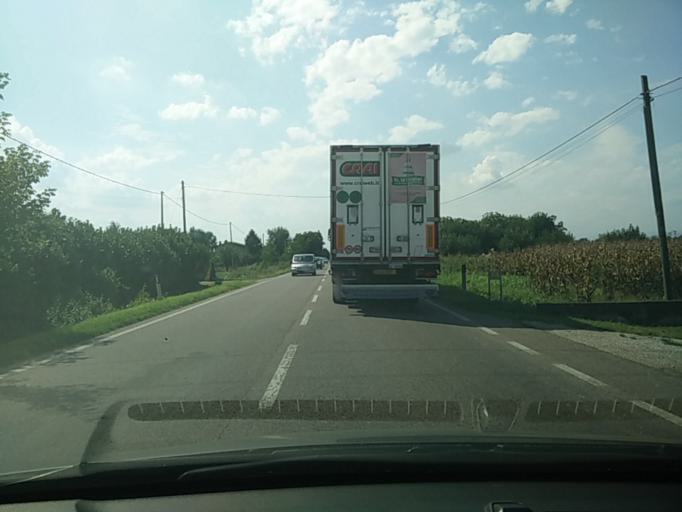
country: IT
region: Veneto
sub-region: Provincia di Treviso
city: Vedelago
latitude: 45.7026
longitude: 12.0278
